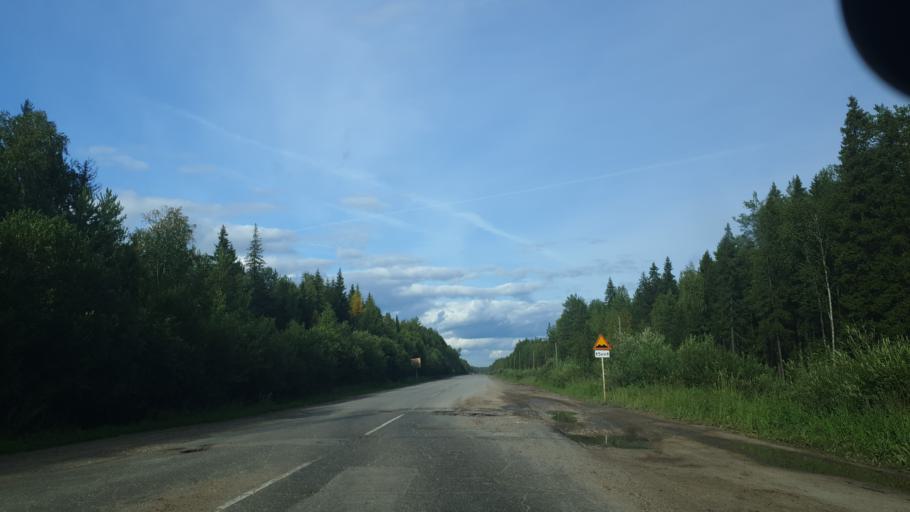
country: RU
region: Komi Republic
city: Ezhva
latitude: 61.7015
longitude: 50.6728
